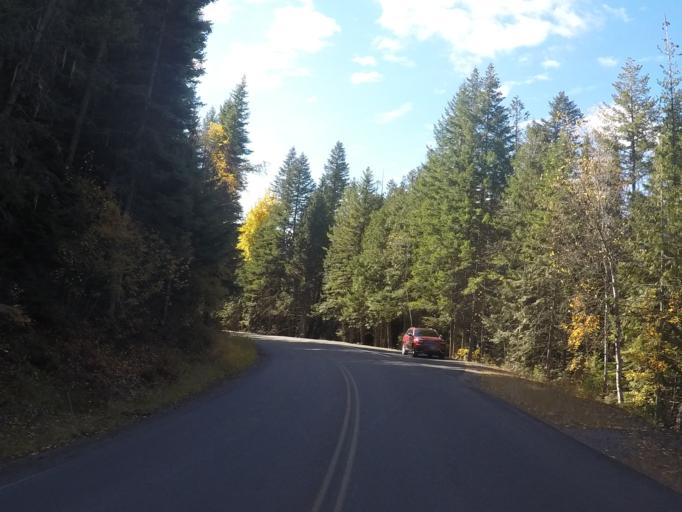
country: US
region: Montana
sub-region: Flathead County
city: Columbia Falls
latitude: 48.5767
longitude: -113.9085
